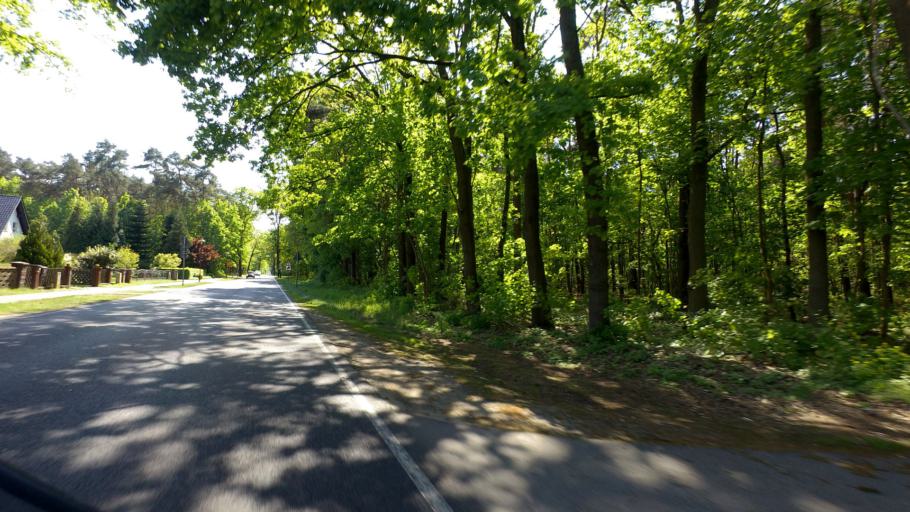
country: DE
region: Brandenburg
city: Tauche
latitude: 52.1133
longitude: 14.1888
